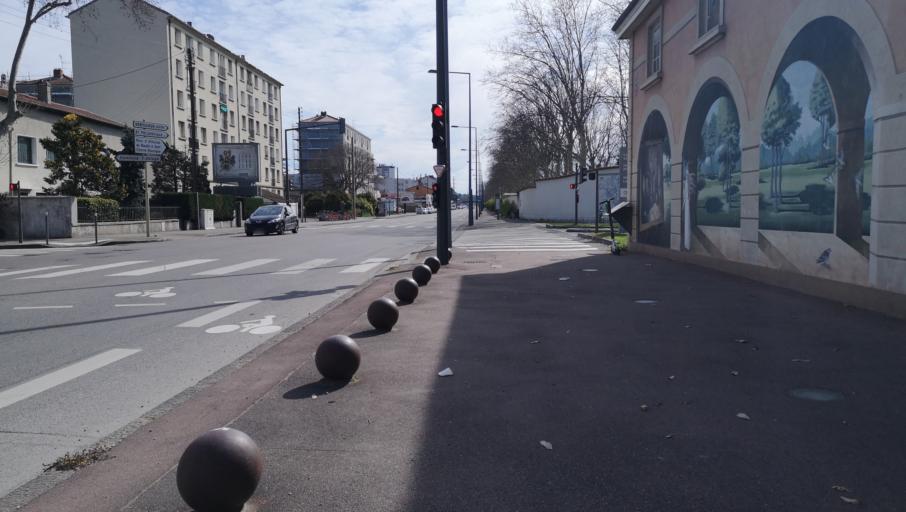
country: FR
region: Rhone-Alpes
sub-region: Departement du Rhone
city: Saint-Fons
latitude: 45.7250
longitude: 4.8539
